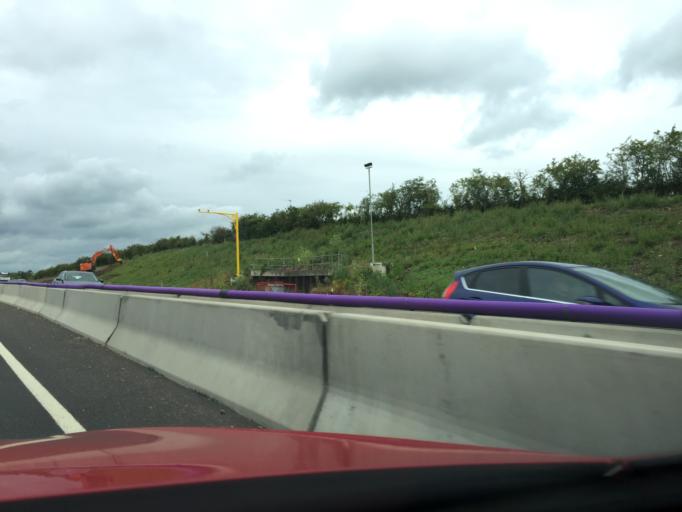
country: GB
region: England
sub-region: Milton Keynes
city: Stoke Goldington
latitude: 52.1153
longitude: -0.7984
